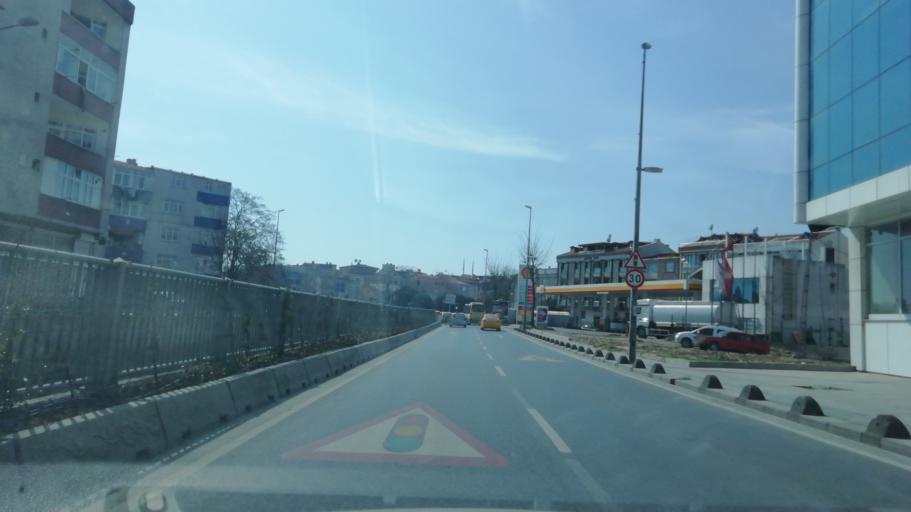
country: TR
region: Istanbul
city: Bagcilar
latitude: 41.0292
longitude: 28.8470
